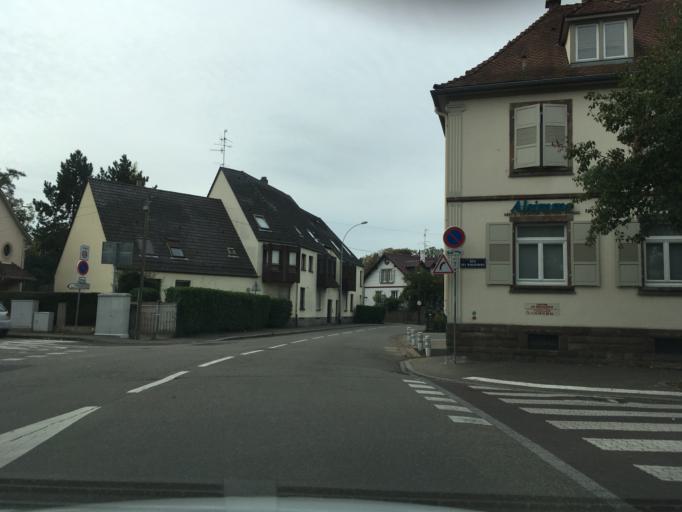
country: FR
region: Alsace
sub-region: Departement du Bas-Rhin
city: Bischheim
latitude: 48.6034
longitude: 7.7868
